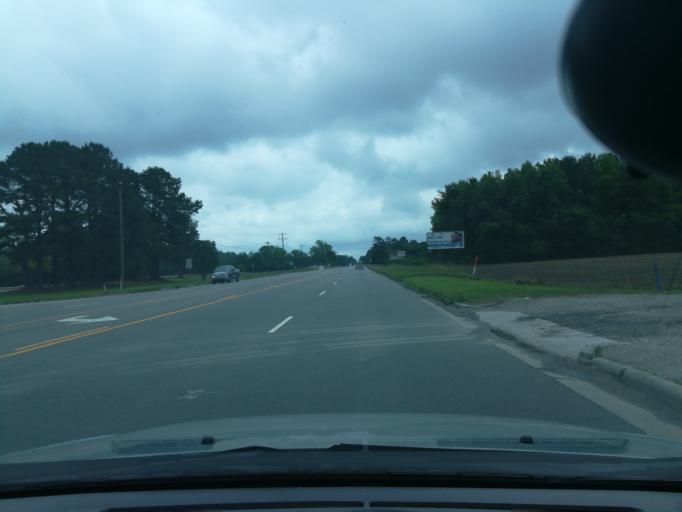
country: US
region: North Carolina
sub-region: Washington County
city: Plymouth
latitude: 35.8717
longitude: -76.6924
